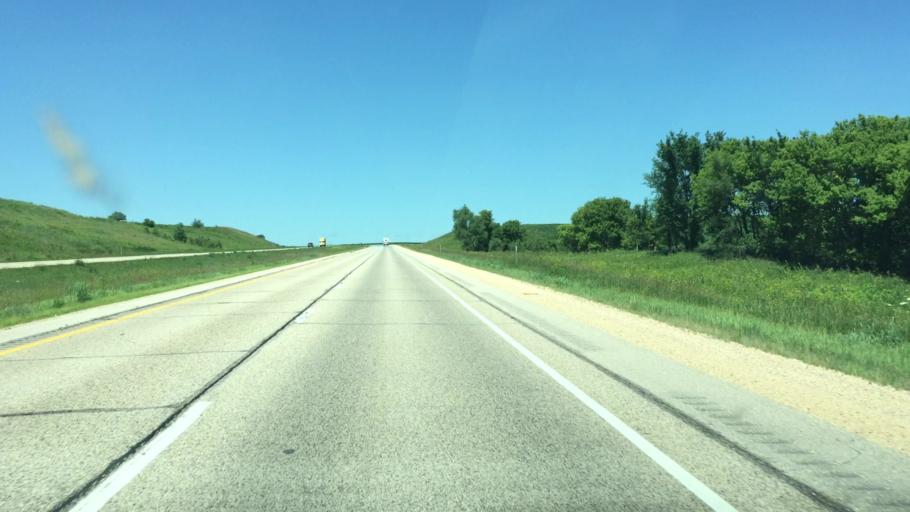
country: US
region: Iowa
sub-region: Jackson County
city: Maquoketa
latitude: 42.1901
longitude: -90.6695
